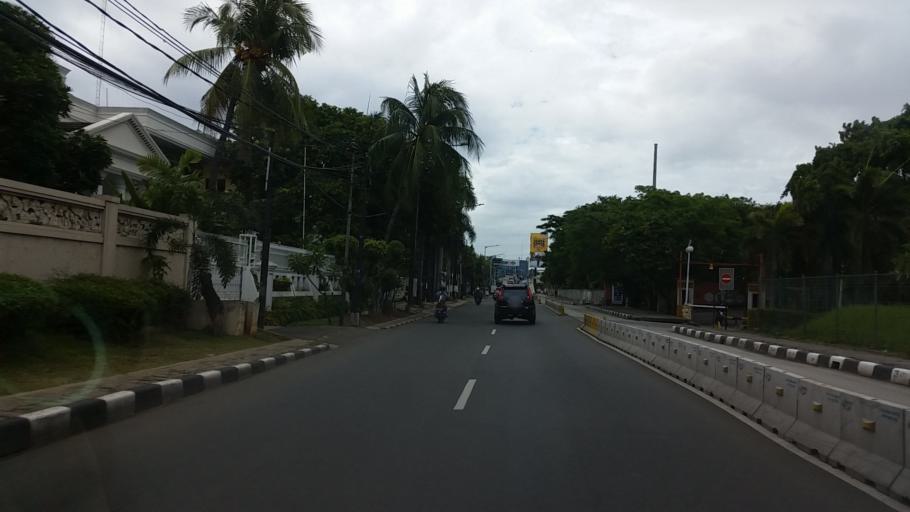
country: ID
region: Jakarta Raya
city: Jakarta
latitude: -6.1175
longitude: 106.7869
